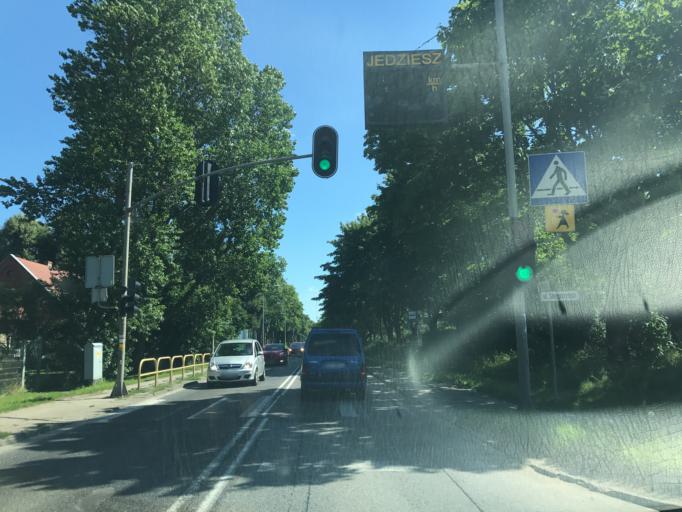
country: PL
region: Pomeranian Voivodeship
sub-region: Powiat gdanski
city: Lublewo Gdanskie
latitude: 54.3529
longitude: 18.4802
